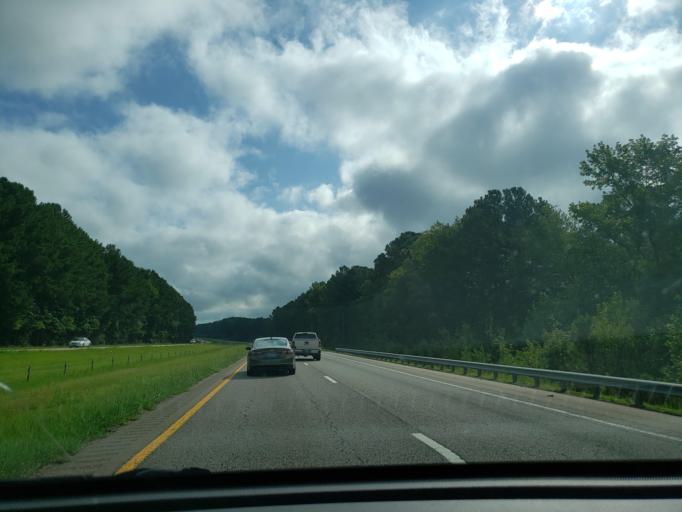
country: US
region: North Carolina
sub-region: Wake County
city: Zebulon
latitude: 35.8700
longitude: -78.2397
